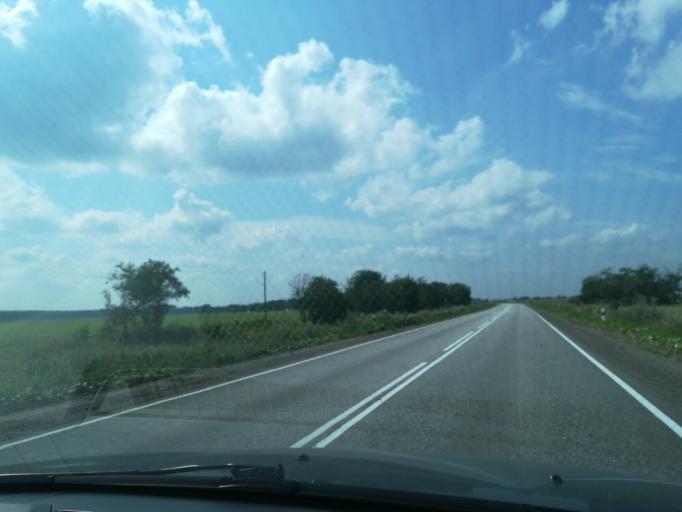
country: RU
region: Leningrad
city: Kopor'ye
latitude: 59.6853
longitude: 29.0373
